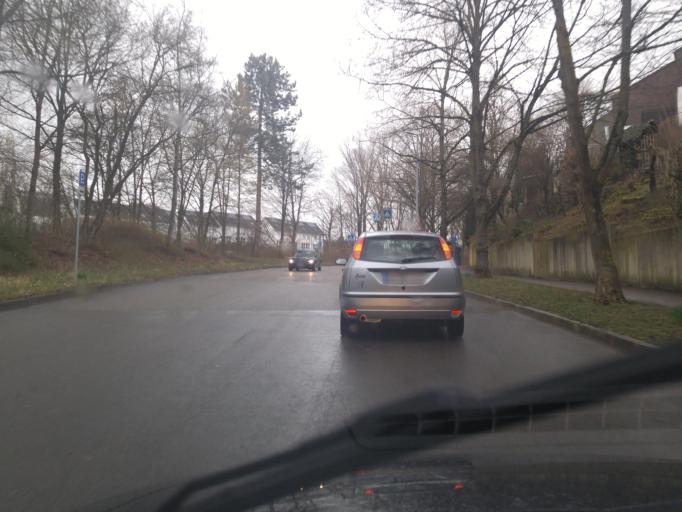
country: DE
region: Baden-Wuerttemberg
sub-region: Regierungsbezirk Stuttgart
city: Waiblingen
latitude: 48.8380
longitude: 9.3285
